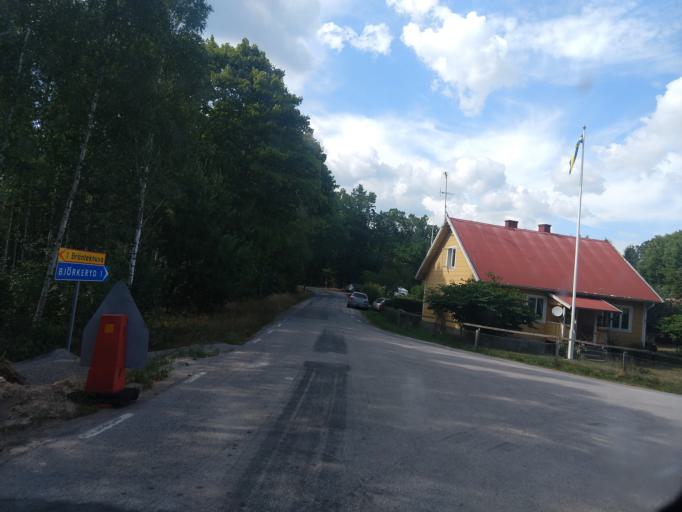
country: SE
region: Blekinge
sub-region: Karlskrona Kommun
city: Nattraby
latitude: 56.2564
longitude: 15.5239
